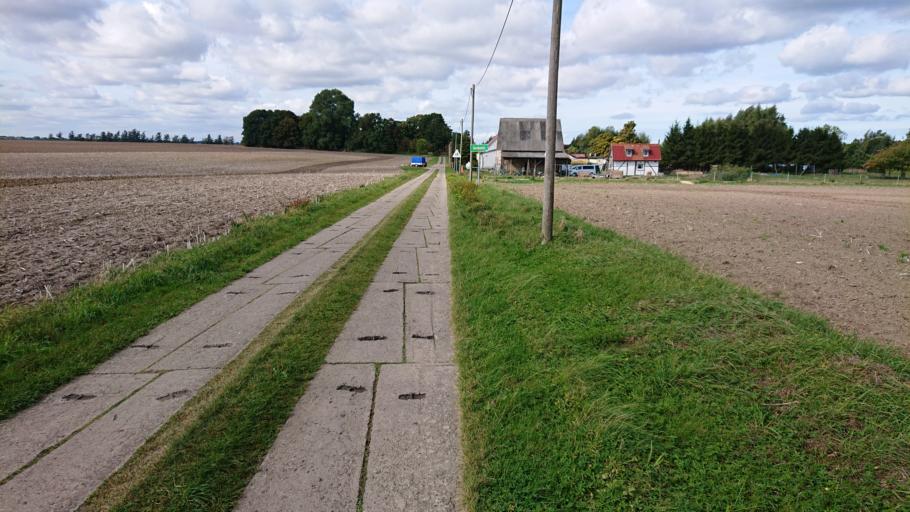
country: DE
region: Mecklenburg-Vorpommern
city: Altefahr
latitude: 54.3506
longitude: 13.1351
